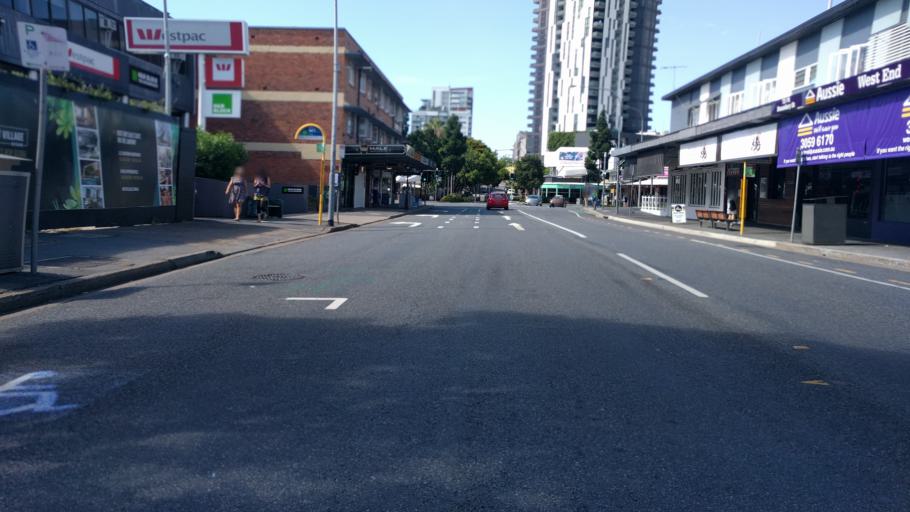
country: AU
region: Queensland
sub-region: Brisbane
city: South Brisbane
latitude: -27.4779
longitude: 153.0126
